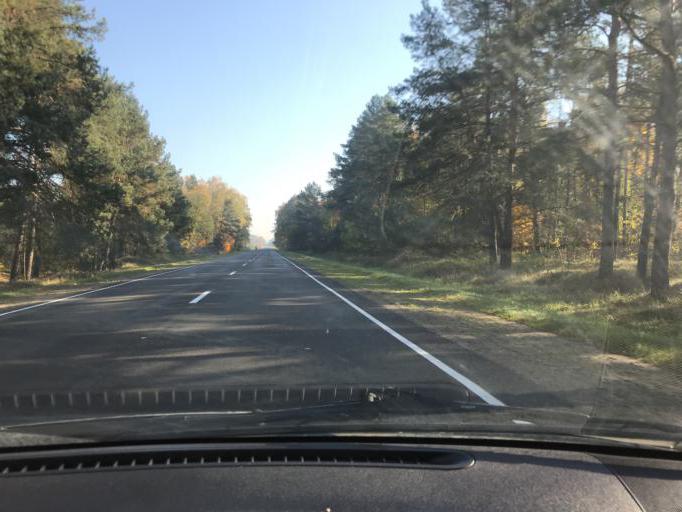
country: BY
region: Brest
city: Baranovichi
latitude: 52.9179
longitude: 25.9653
